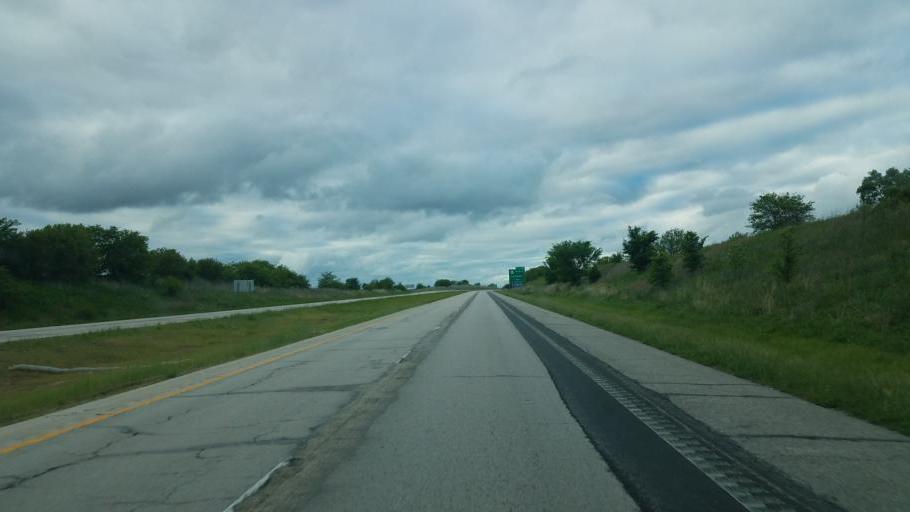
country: US
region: Iowa
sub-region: Decatur County
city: Lamoni
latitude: 40.5588
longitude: -93.9506
